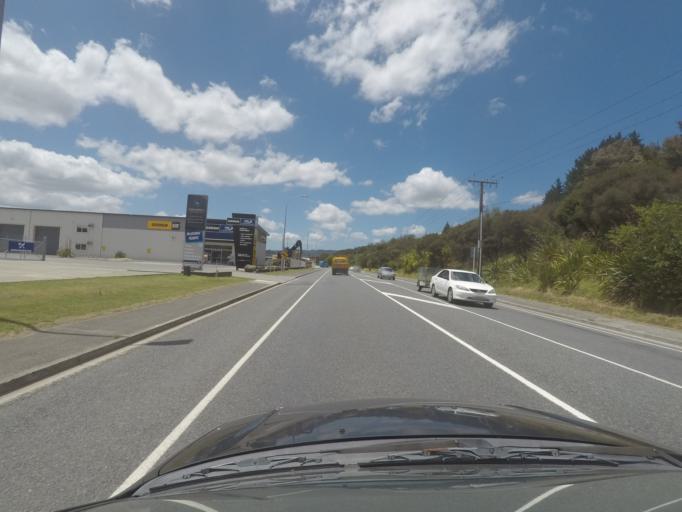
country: NZ
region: Northland
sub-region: Whangarei
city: Whangarei
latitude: -35.7432
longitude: 174.3293
